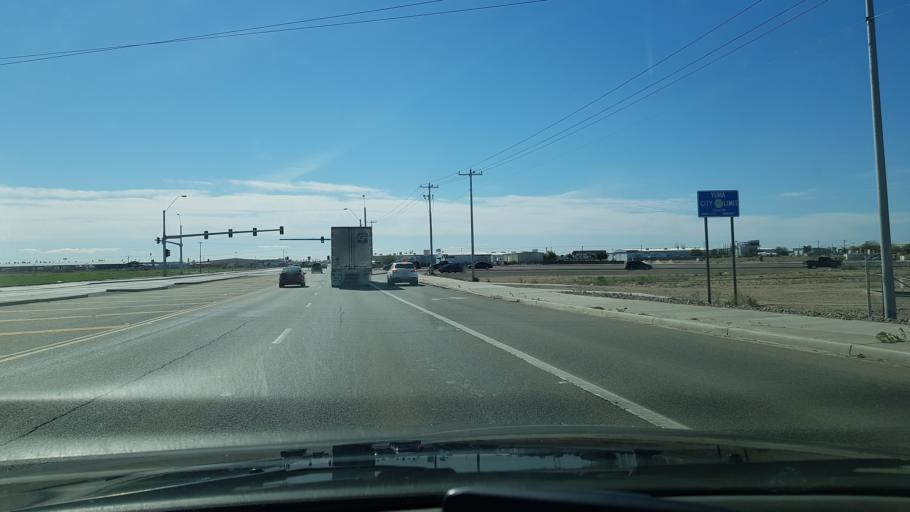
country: US
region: Arizona
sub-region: Yuma County
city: Yuma
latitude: 32.6812
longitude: -114.5818
